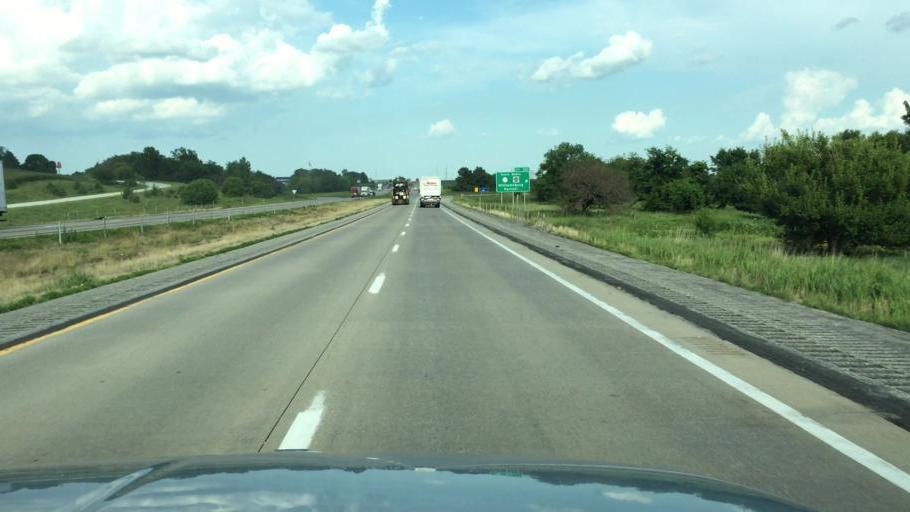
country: US
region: Iowa
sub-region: Iowa County
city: Williamsburg
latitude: 41.6870
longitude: -92.0168
